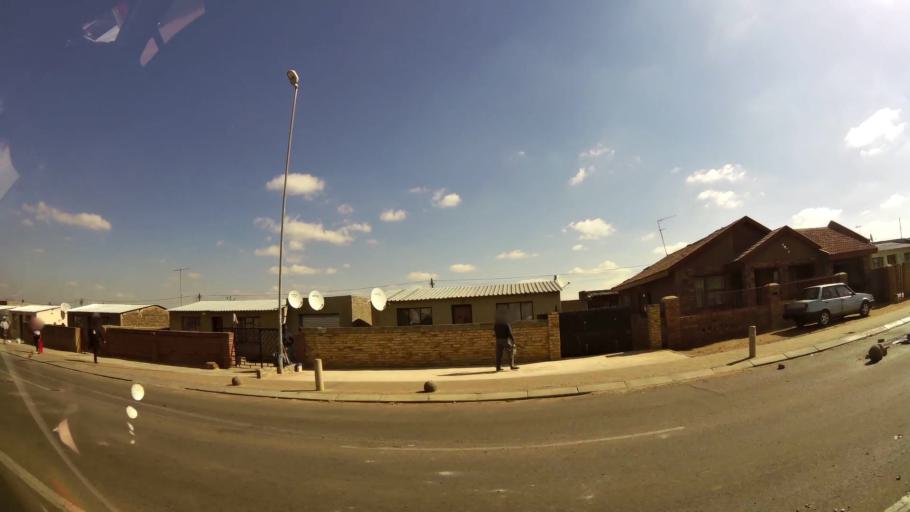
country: ZA
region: Gauteng
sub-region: West Rand District Municipality
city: Krugersdorp
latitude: -26.1601
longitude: 27.7821
